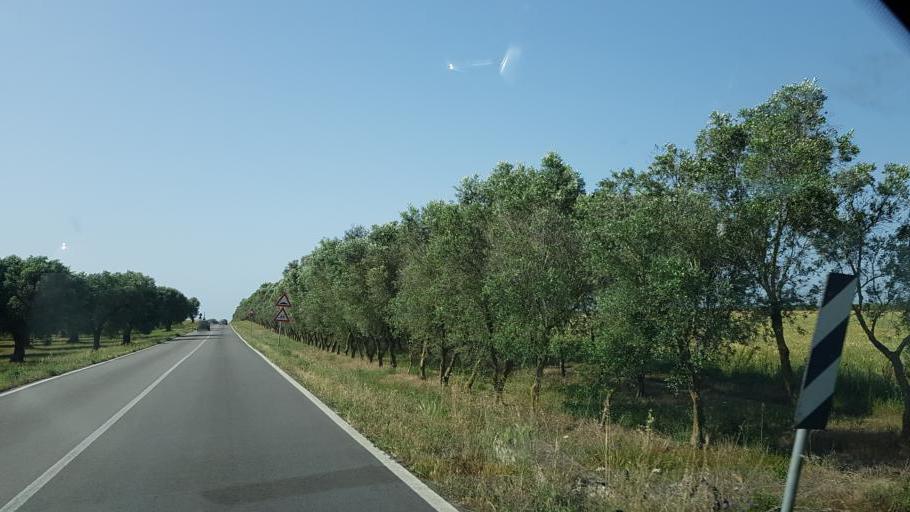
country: IT
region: Apulia
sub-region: Provincia di Brindisi
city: San Pancrazio Salentino
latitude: 40.3711
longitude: 17.8393
